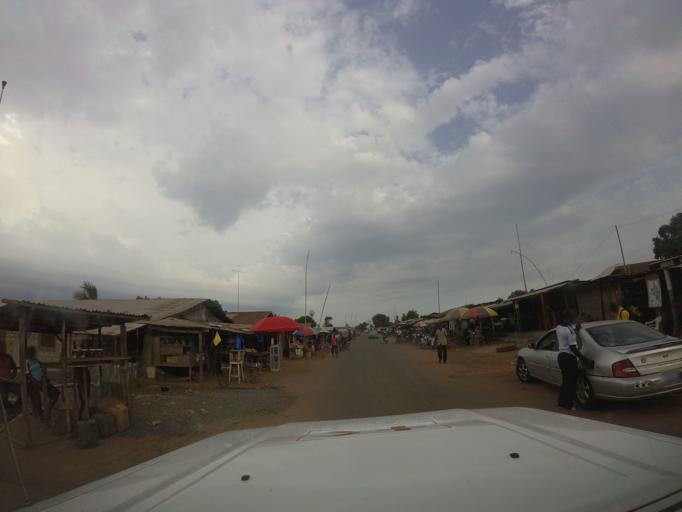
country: LR
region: Bomi
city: Tubmanburg
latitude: 6.7151
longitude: -10.9724
